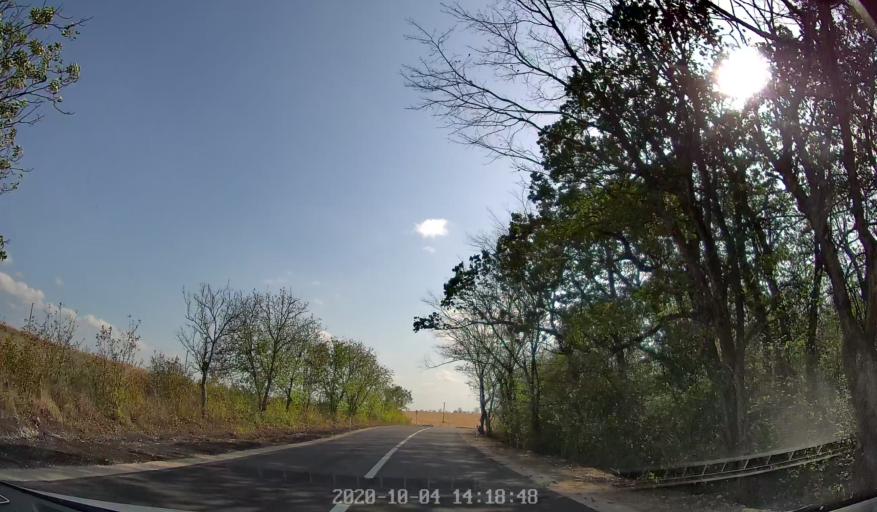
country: MD
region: Rezina
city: Saharna
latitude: 47.5965
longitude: 28.9767
